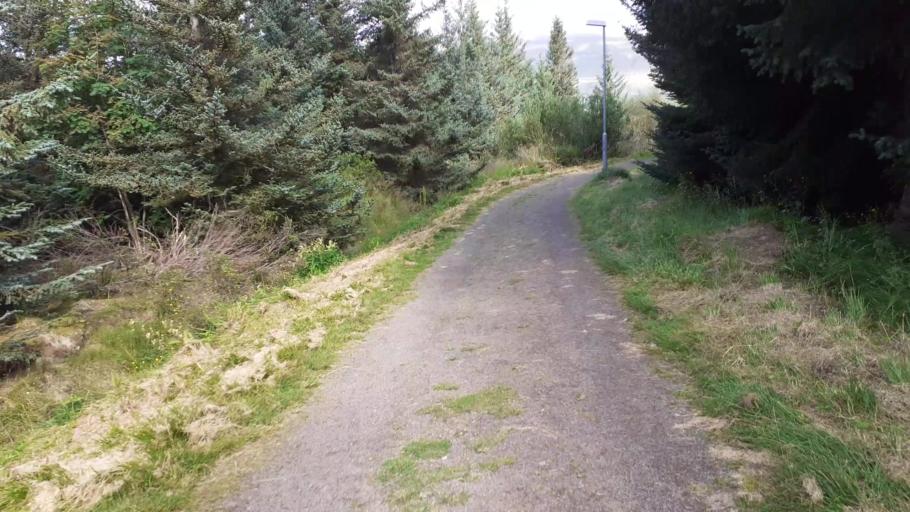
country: IS
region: Northeast
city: Akureyri
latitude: 65.6417
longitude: -18.0957
